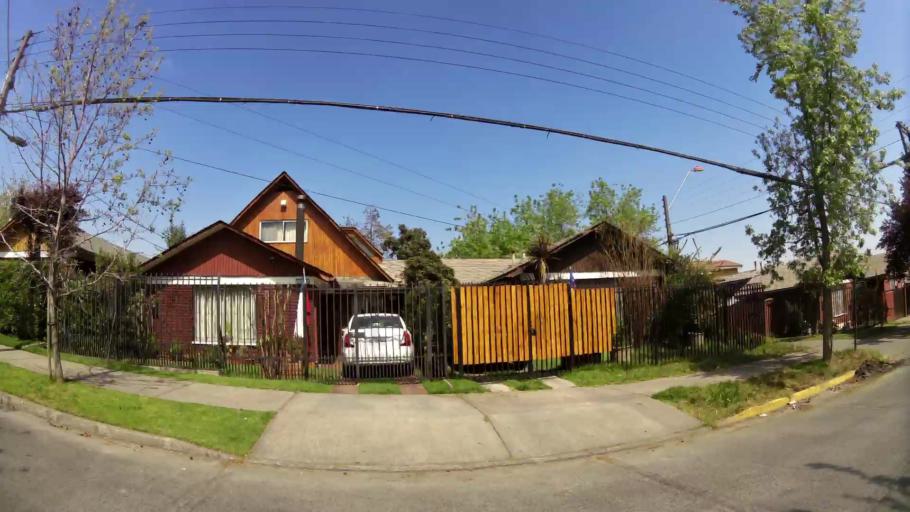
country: CL
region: Santiago Metropolitan
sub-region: Provincia de Santiago
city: Villa Presidente Frei, Nunoa, Santiago, Chile
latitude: -33.4646
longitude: -70.5437
